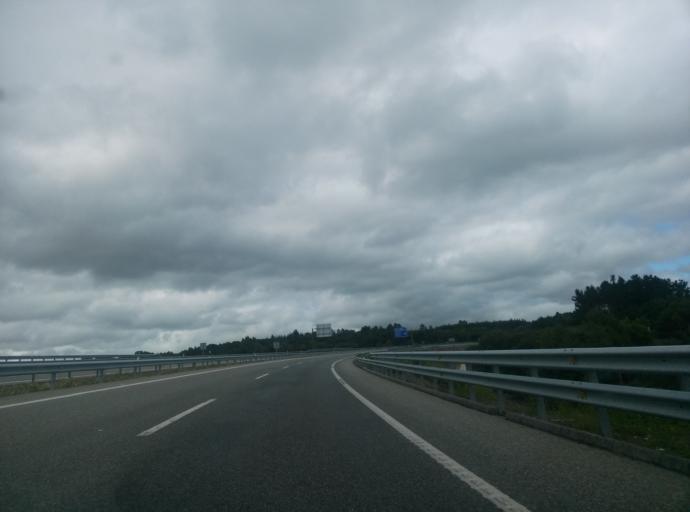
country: ES
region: Galicia
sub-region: Provincia de Lugo
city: Vilalba
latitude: 43.3101
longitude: -7.7062
